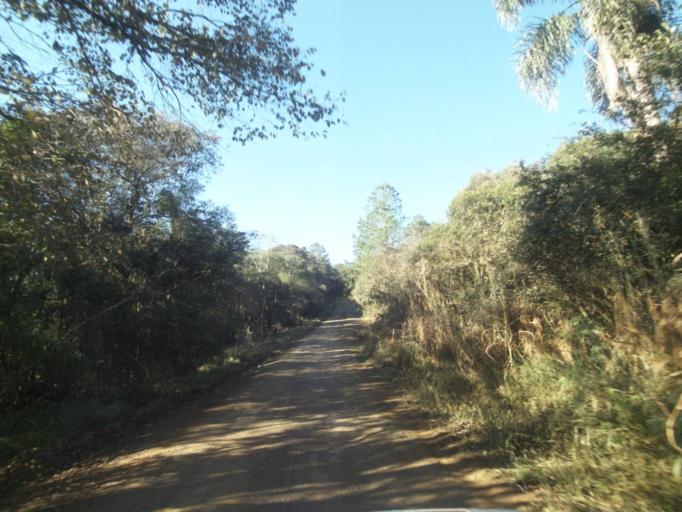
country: BR
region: Parana
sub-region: Tibagi
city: Tibagi
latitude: -24.5409
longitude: -50.5031
